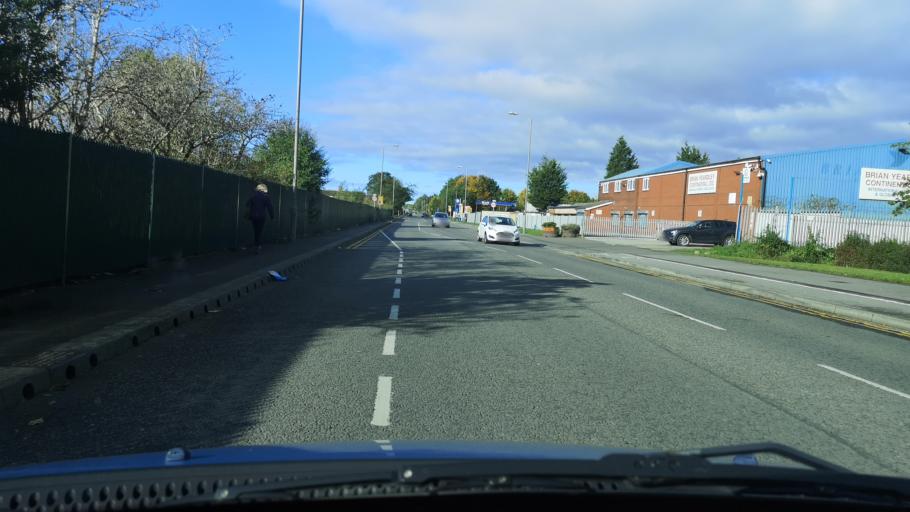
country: GB
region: England
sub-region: City and Borough of Wakefield
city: Featherstone
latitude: 53.6752
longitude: -1.3655
